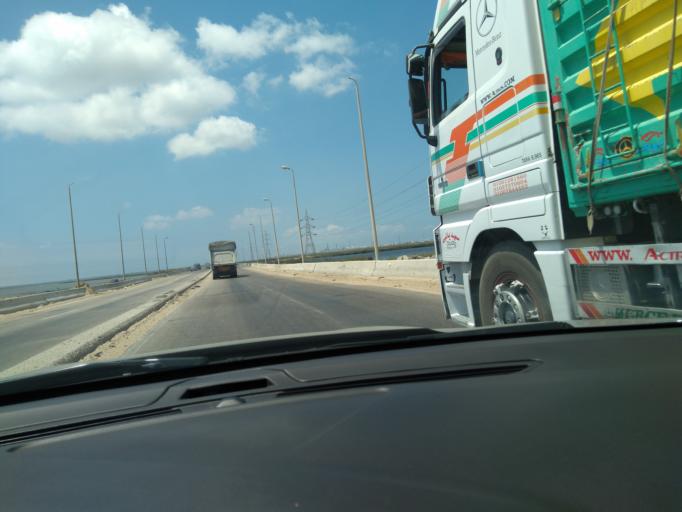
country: EG
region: Muhafazat Bur Sa`id
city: Port Said
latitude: 31.2712
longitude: 32.2097
